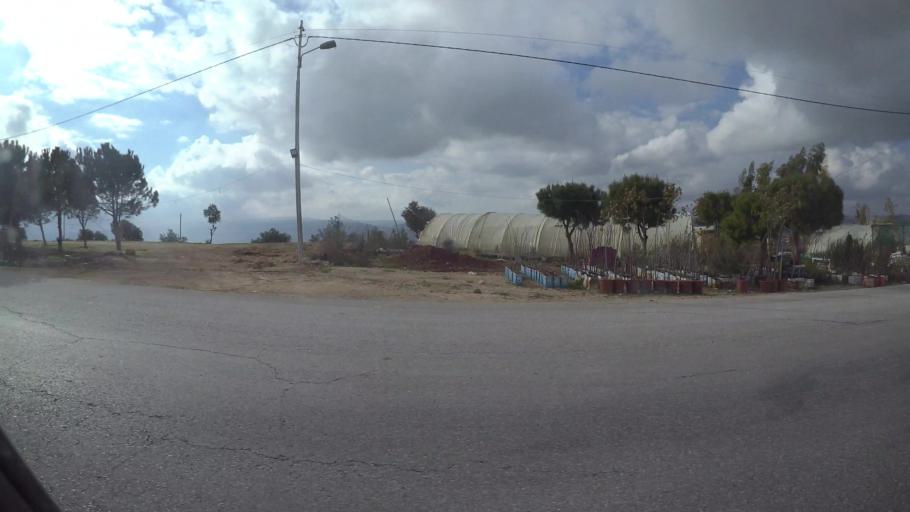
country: JO
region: Amman
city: Al Jubayhah
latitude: 32.0737
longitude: 35.8781
